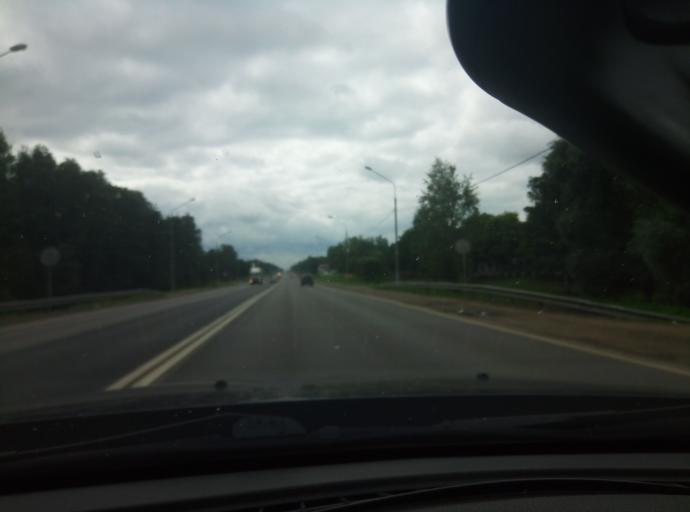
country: RU
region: Kaluga
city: Obninsk
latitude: 55.0983
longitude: 36.6382
